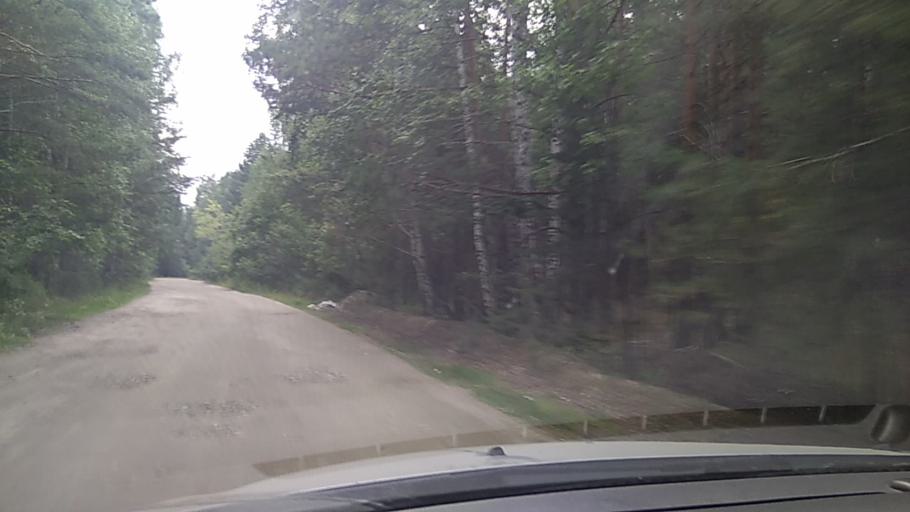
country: RU
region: Chelyabinsk
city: Kyshtym
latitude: 55.6788
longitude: 60.5823
